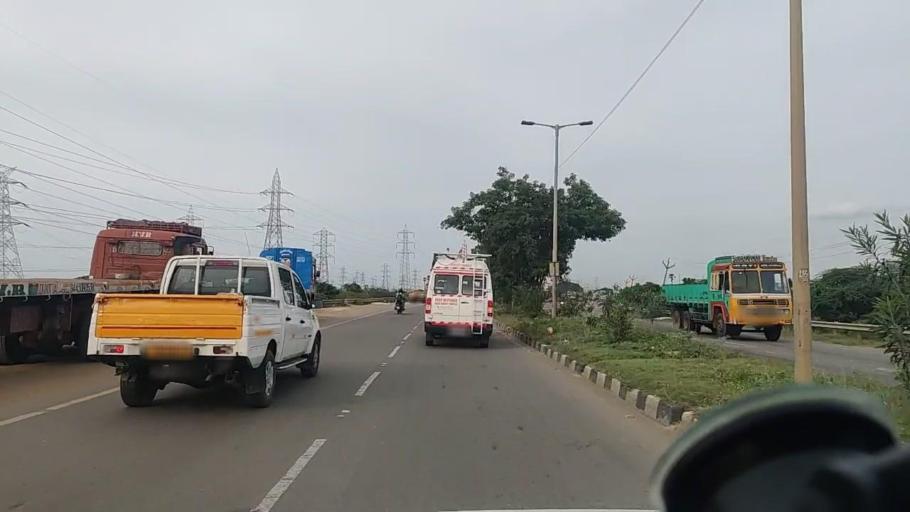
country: IN
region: Tamil Nadu
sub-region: Thiruvallur
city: Chinnasekkadu
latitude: 13.1722
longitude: 80.2346
